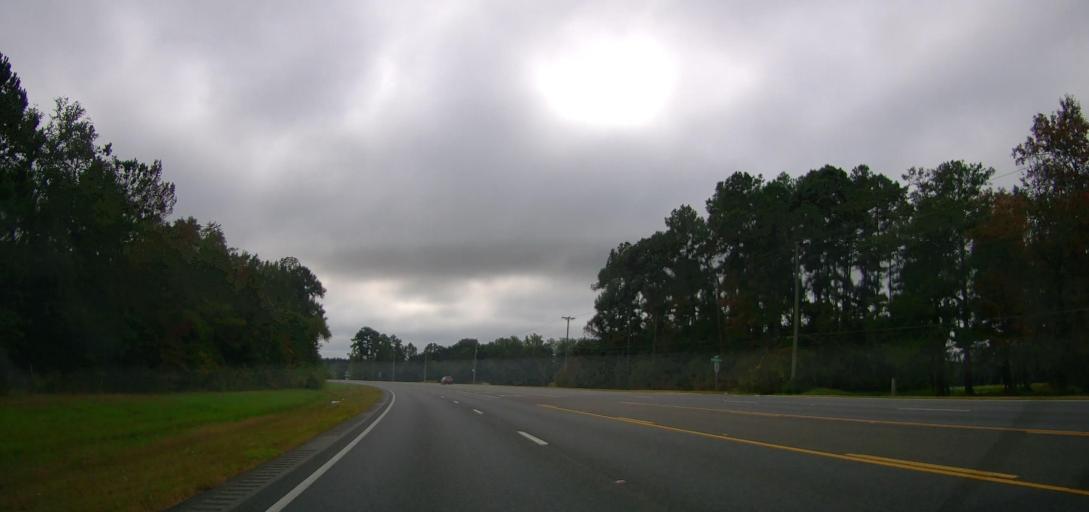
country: US
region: Georgia
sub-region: Thomas County
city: Thomasville
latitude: 30.8949
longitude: -83.9317
